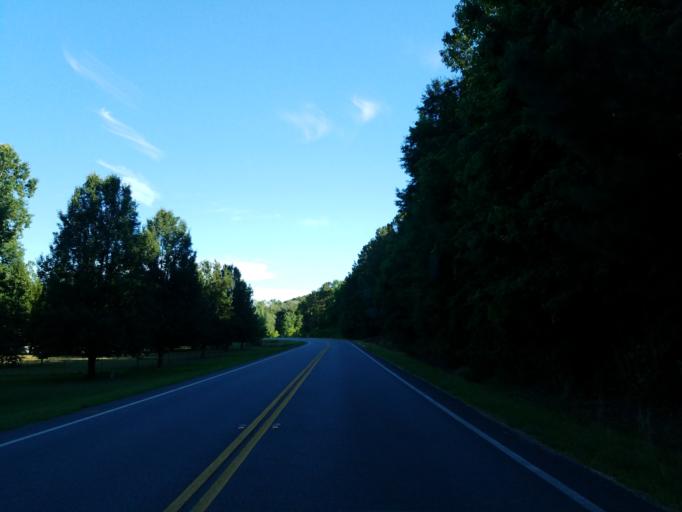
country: US
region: Georgia
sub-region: Gordon County
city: Calhoun
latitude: 34.5988
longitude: -85.0421
